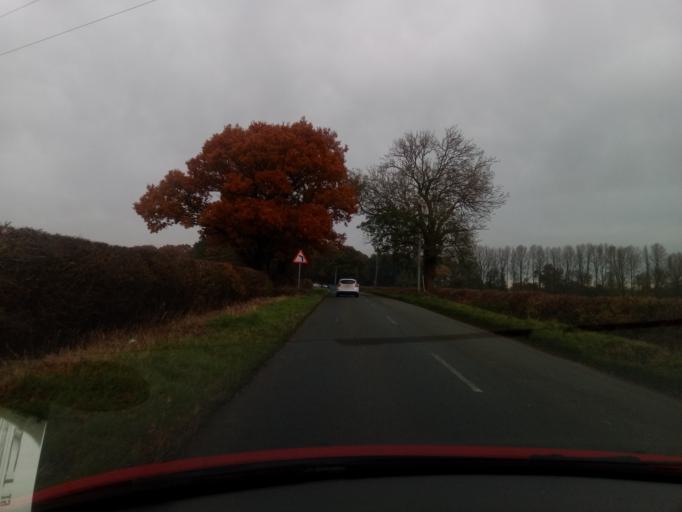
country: GB
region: England
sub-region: Derbyshire
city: Borrowash
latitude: 52.9338
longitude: -1.4032
